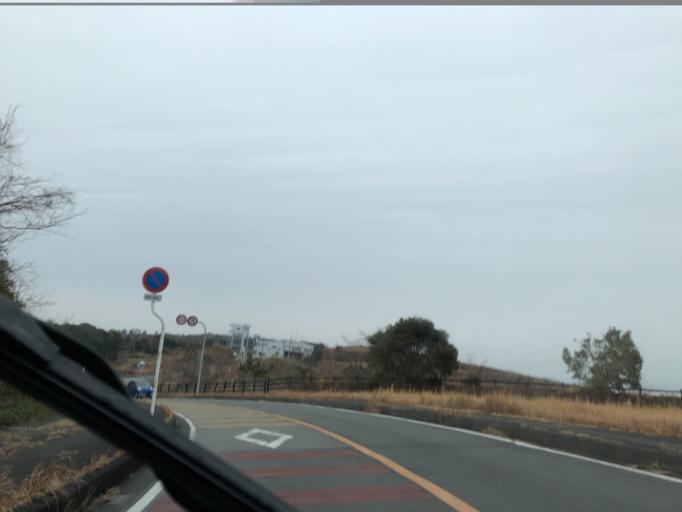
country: JP
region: Wakayama
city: Tanabe
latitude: 33.6664
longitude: 135.3583
